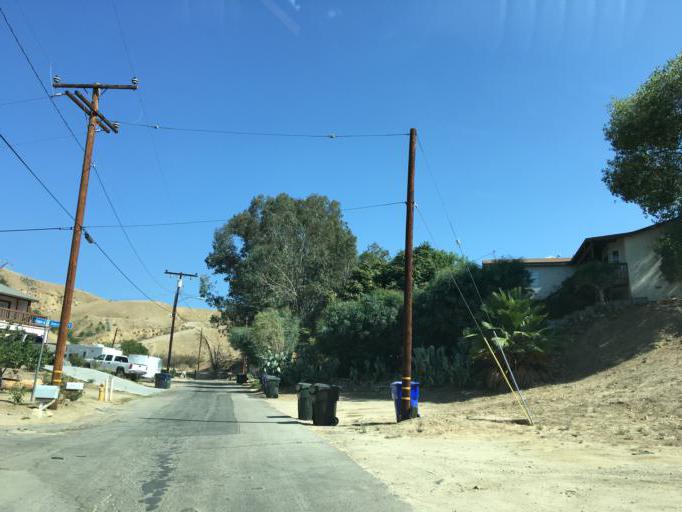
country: US
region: California
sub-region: Los Angeles County
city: Val Verde
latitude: 34.4522
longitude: -118.6640
